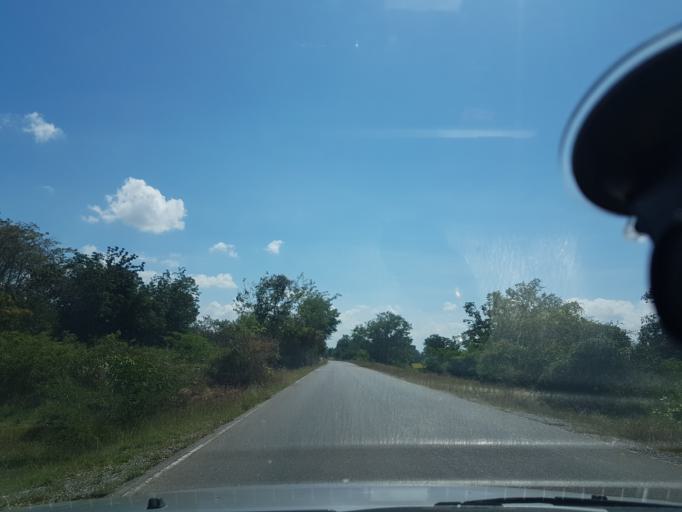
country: TH
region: Lop Buri
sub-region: Amphoe Tha Luang
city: Tha Luang
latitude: 15.0071
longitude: 100.9988
